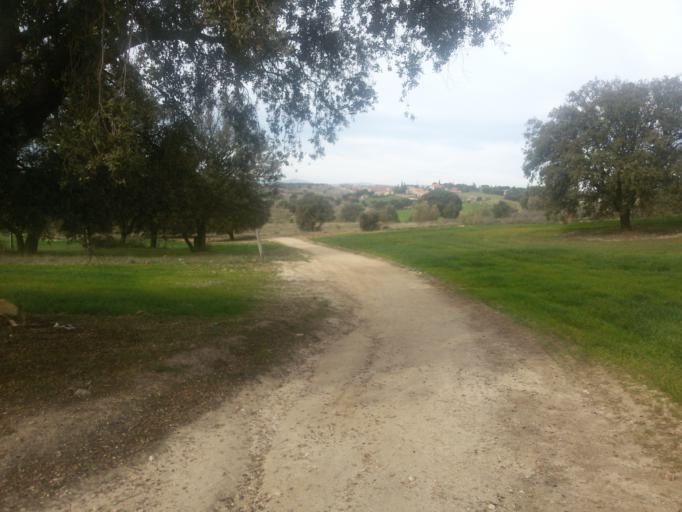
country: ES
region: Madrid
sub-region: Provincia de Madrid
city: Sevilla La Nueva
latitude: 40.3351
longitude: -4.0258
